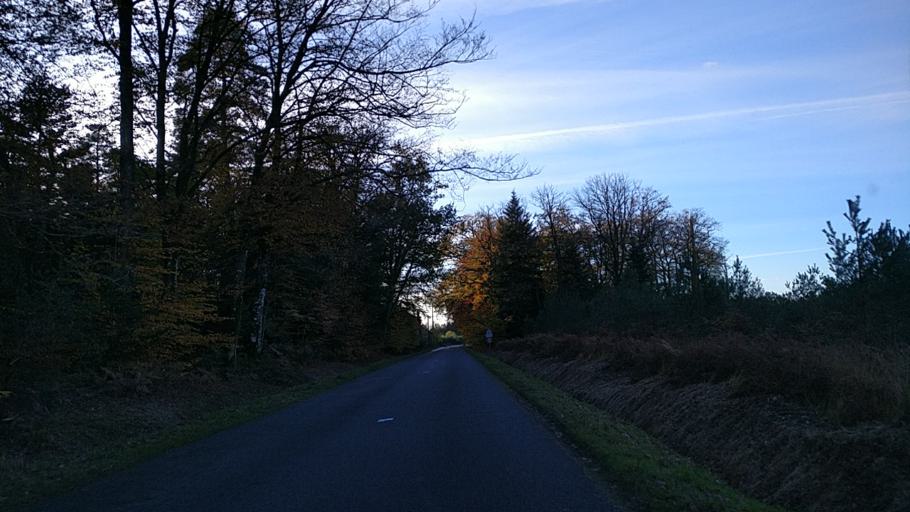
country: FR
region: Brittany
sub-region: Departement d'Ille-et-Vilaine
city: Liffre
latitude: 48.1890
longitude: -1.5424
